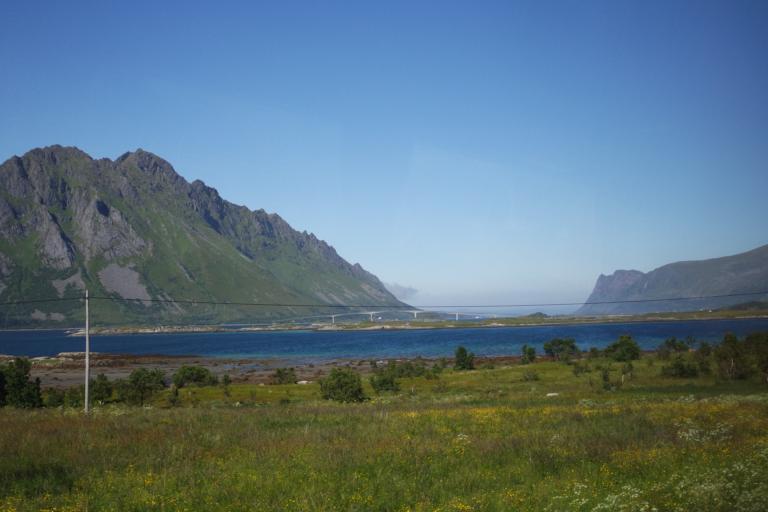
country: NO
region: Nordland
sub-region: Vagan
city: Kabelvag
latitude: 68.2329
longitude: 14.2352
